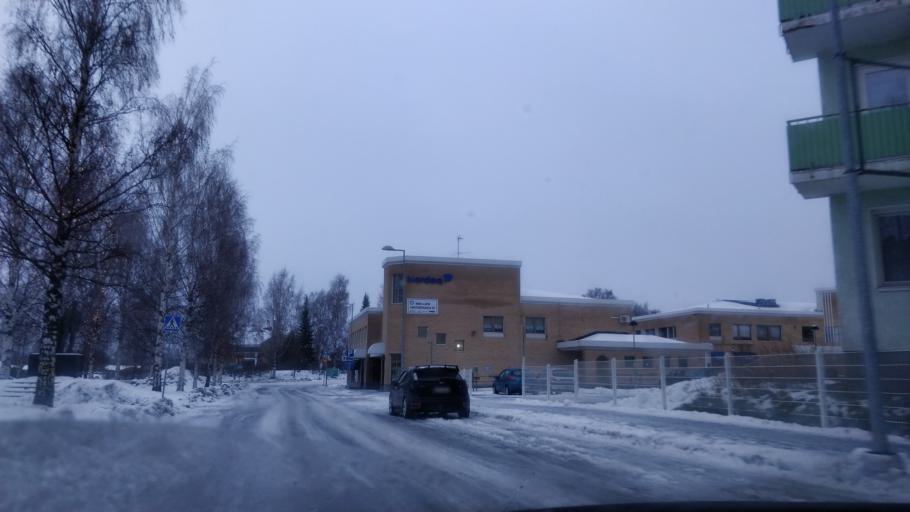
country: FI
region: Lapland
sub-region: Kemi-Tornio
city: Kemi
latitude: 65.7379
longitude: 24.5611
